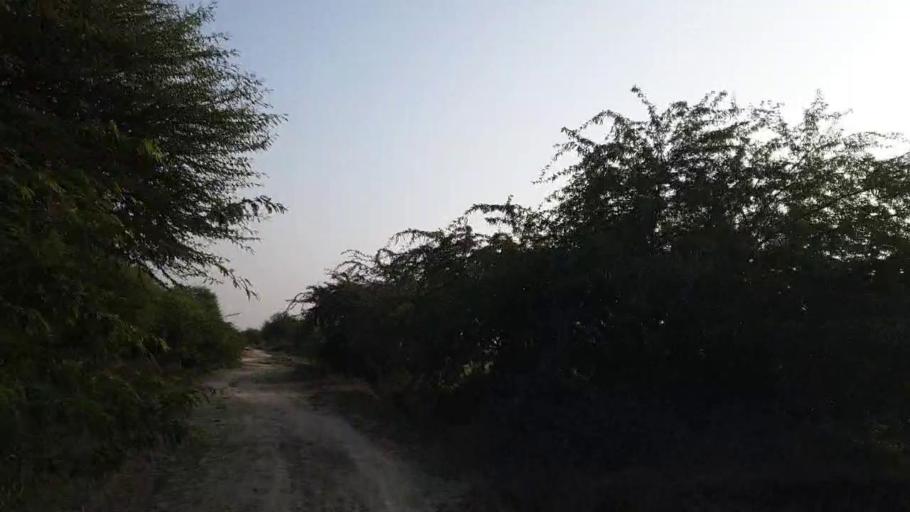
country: PK
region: Sindh
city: Kario
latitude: 24.8710
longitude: 68.6208
